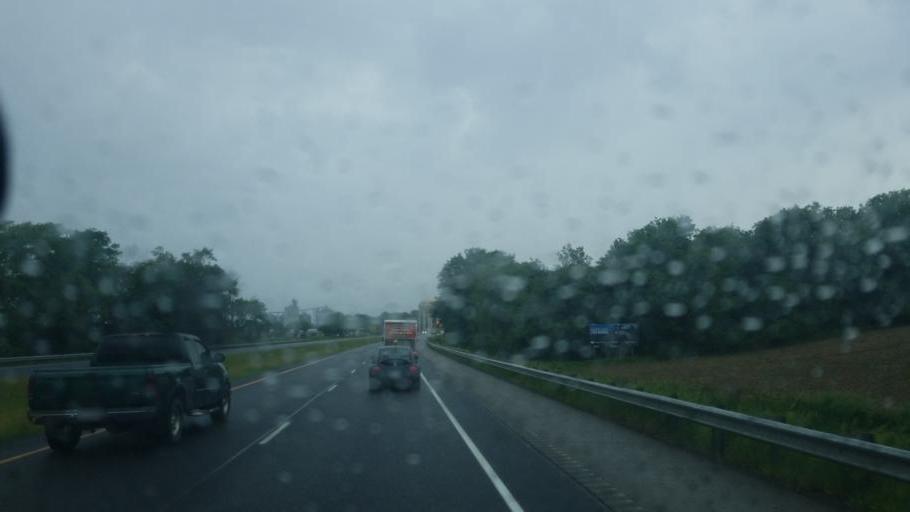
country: US
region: Indiana
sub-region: Whitley County
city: Churubusco
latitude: 41.1263
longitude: -85.3693
